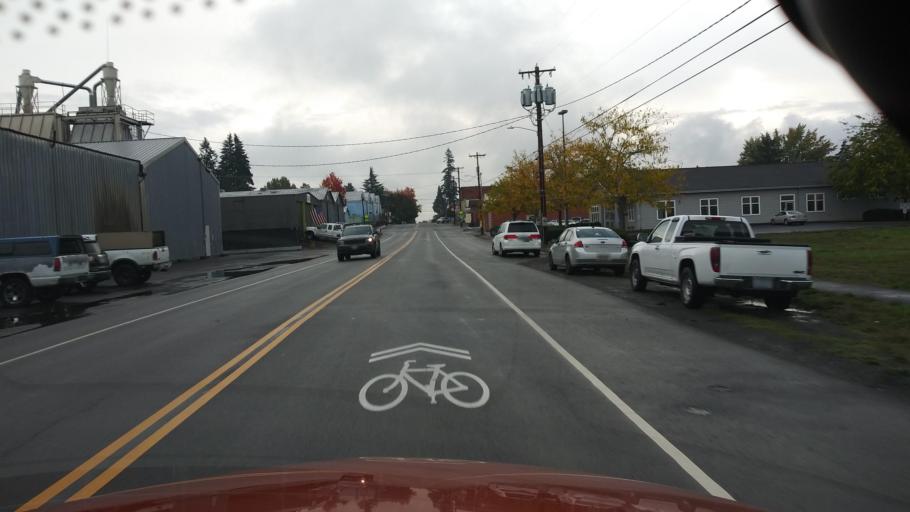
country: US
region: Oregon
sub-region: Washington County
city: North Plains
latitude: 45.5981
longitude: -123.0045
